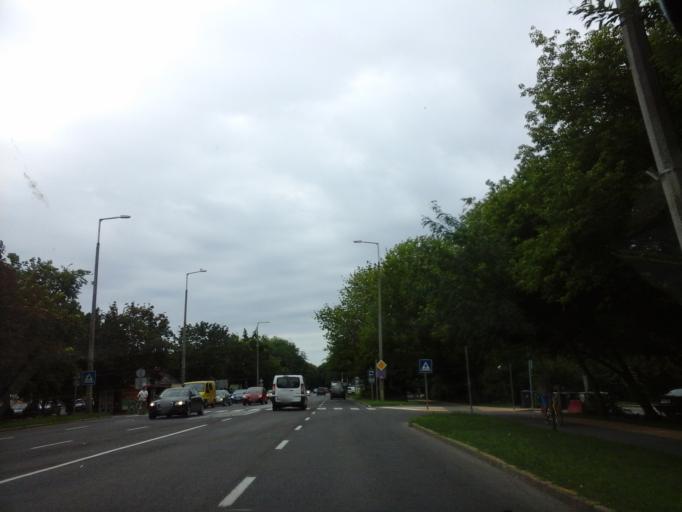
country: HU
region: Hajdu-Bihar
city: Hajduszoboszlo
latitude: 47.4488
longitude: 21.4017
